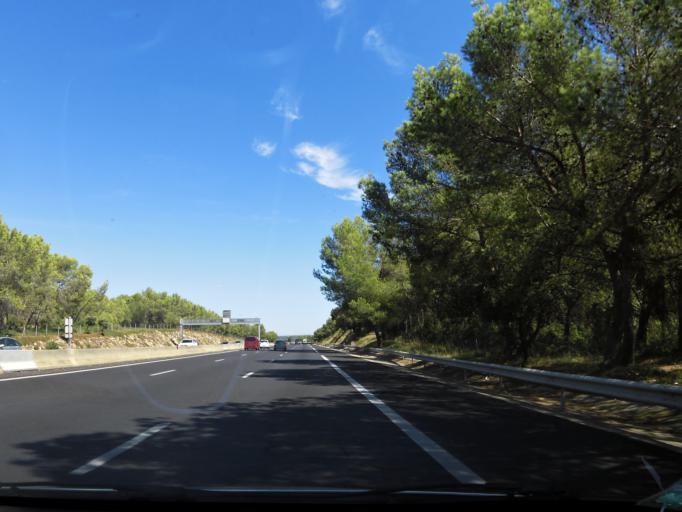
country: FR
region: Languedoc-Roussillon
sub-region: Departement du Gard
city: Vergeze
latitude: 43.7494
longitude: 4.2341
